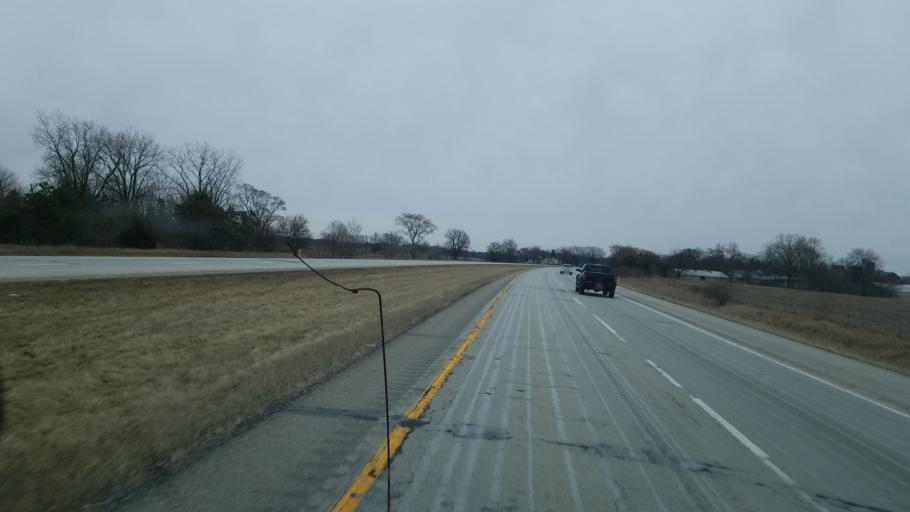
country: US
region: Indiana
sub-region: Starke County
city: Knox
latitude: 41.3927
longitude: -86.5920
